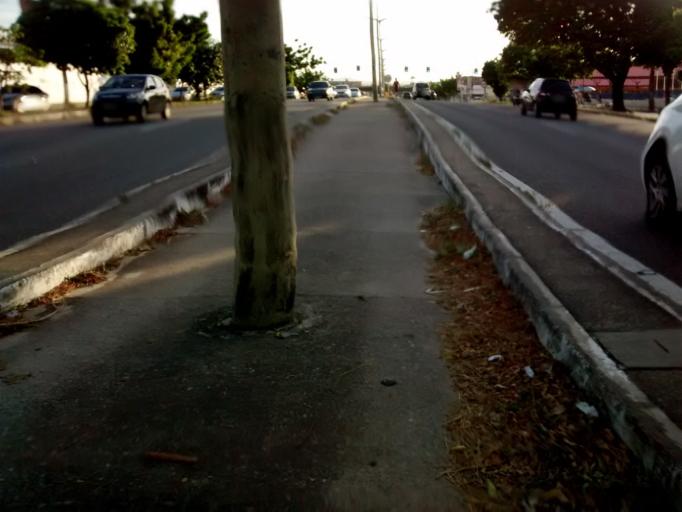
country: BR
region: Ceara
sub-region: Fortaleza
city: Fortaleza
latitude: -3.7383
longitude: -38.5821
